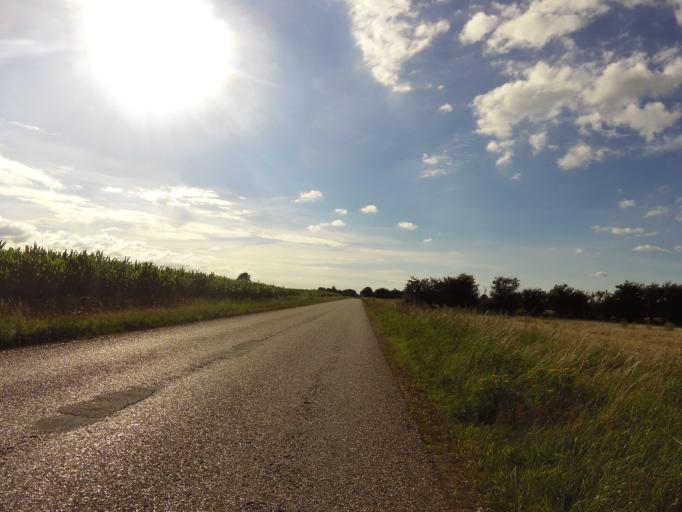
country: DK
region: South Denmark
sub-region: Haderslev Kommune
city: Vojens
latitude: 55.2019
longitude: 9.2882
